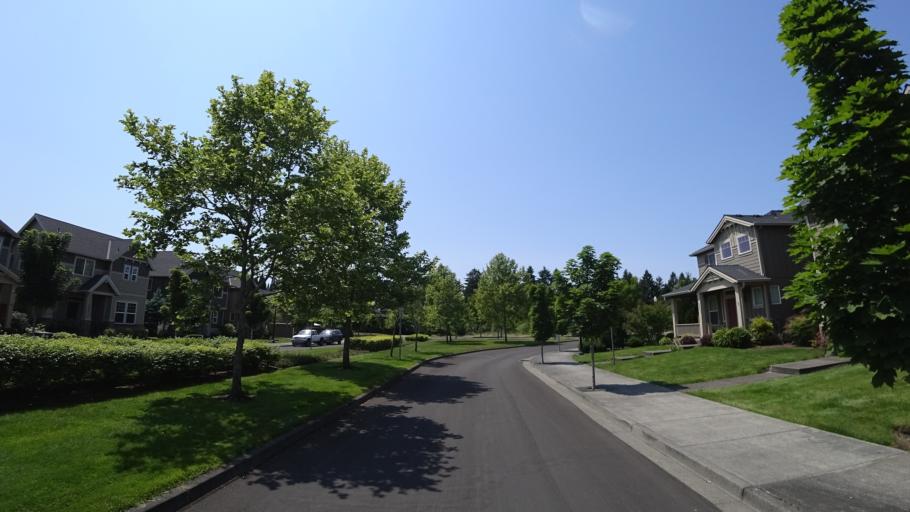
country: US
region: Oregon
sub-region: Washington County
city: Hillsboro
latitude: 45.4962
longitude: -122.9354
